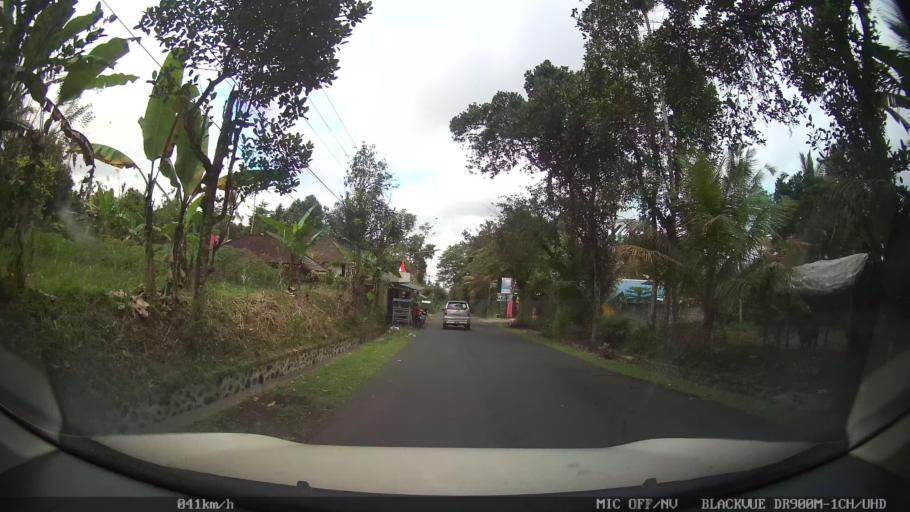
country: ID
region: Bali
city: Banjar Geriana Kangin
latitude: -8.3988
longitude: 115.4334
